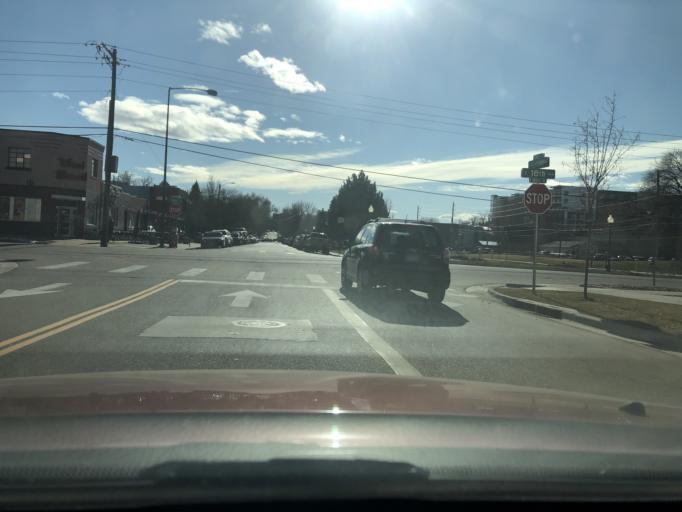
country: US
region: Colorado
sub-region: Denver County
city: Denver
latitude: 39.7451
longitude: -104.9697
